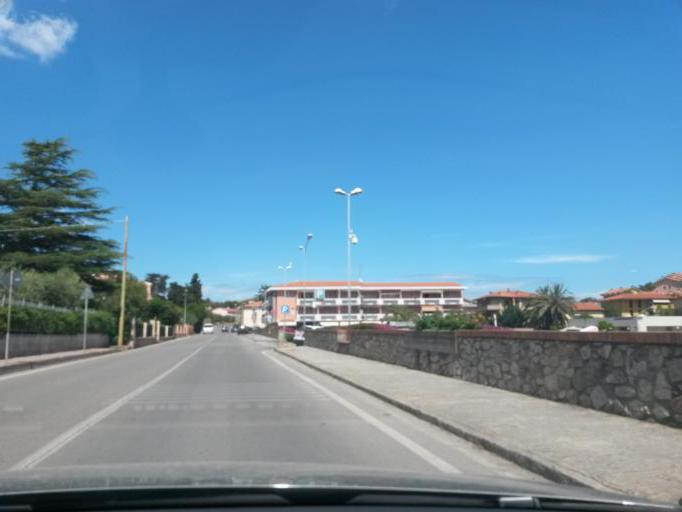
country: IT
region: Tuscany
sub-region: Provincia di Livorno
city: Porto Azzurro
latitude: 42.7679
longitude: 10.3950
